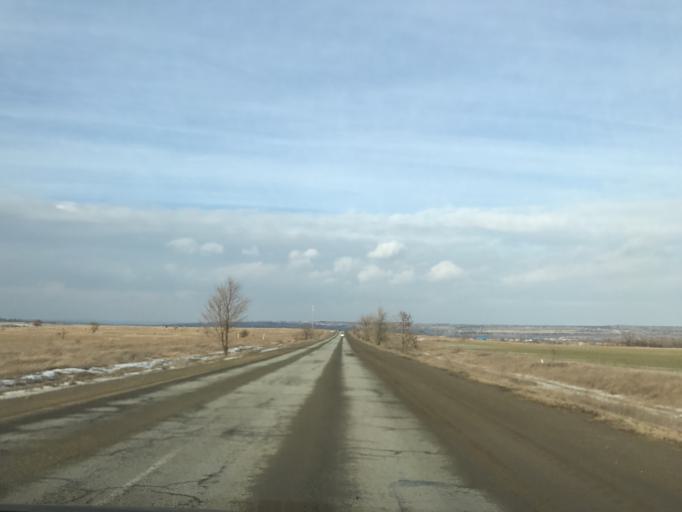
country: RU
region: Rostov
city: Staraya Stanitsa
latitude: 48.2754
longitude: 40.3462
